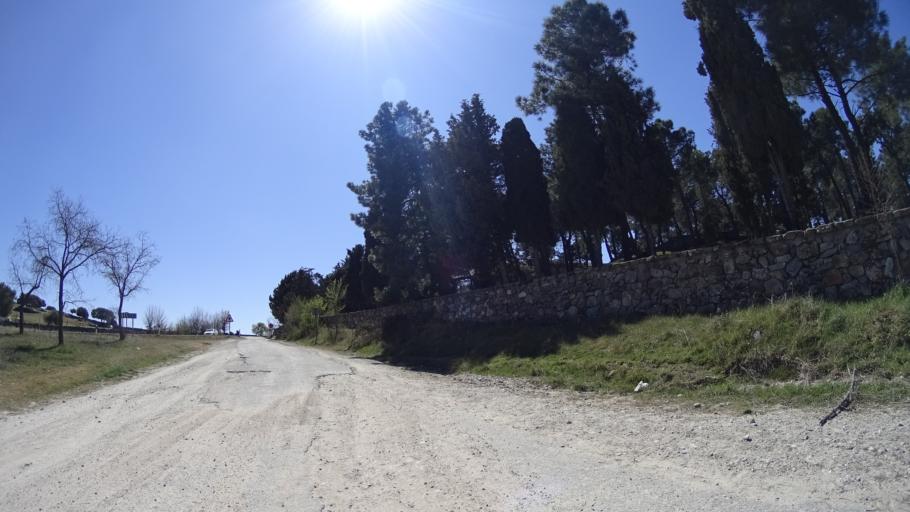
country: ES
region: Madrid
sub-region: Provincia de Madrid
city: Colmenar Viejo
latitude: 40.7038
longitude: -3.7692
